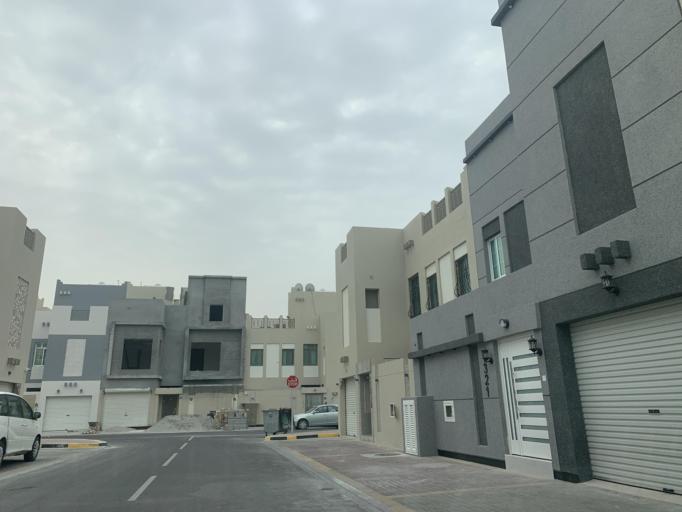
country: BH
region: Northern
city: Madinat `Isa
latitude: 26.1788
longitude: 50.5164
